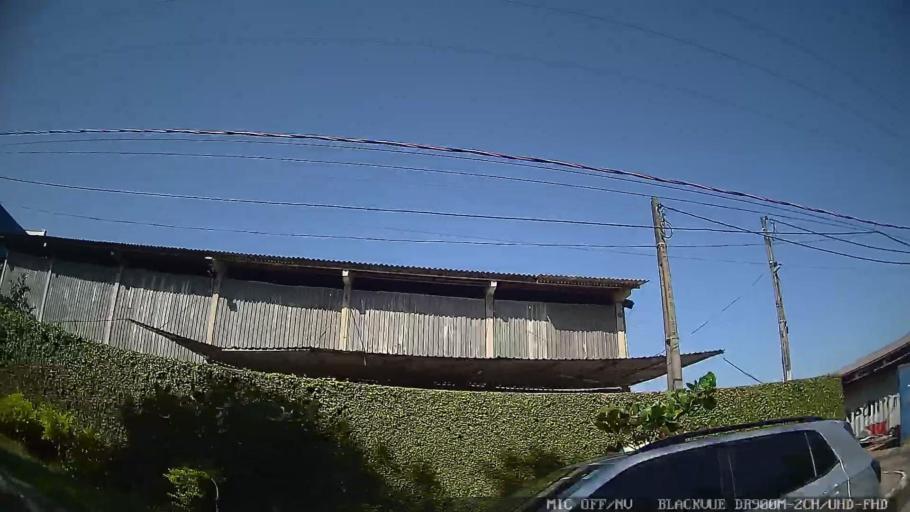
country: BR
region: Sao Paulo
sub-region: Guaruja
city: Guaruja
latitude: -24.0039
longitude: -46.2926
